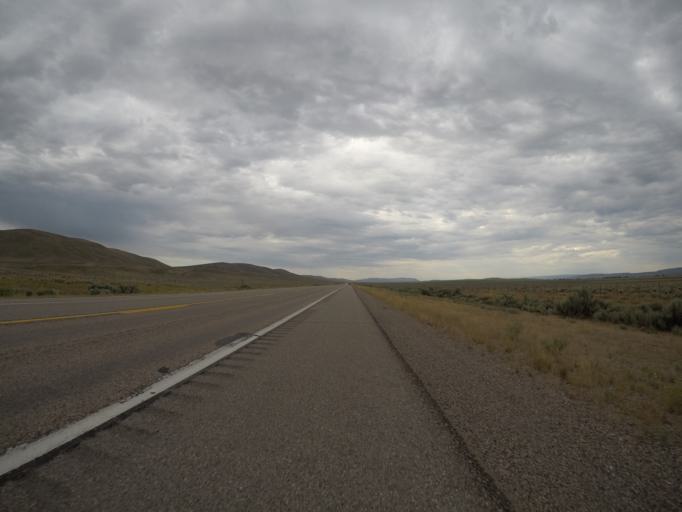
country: US
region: Utah
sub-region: Rich County
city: Randolph
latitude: 41.8894
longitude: -110.9619
